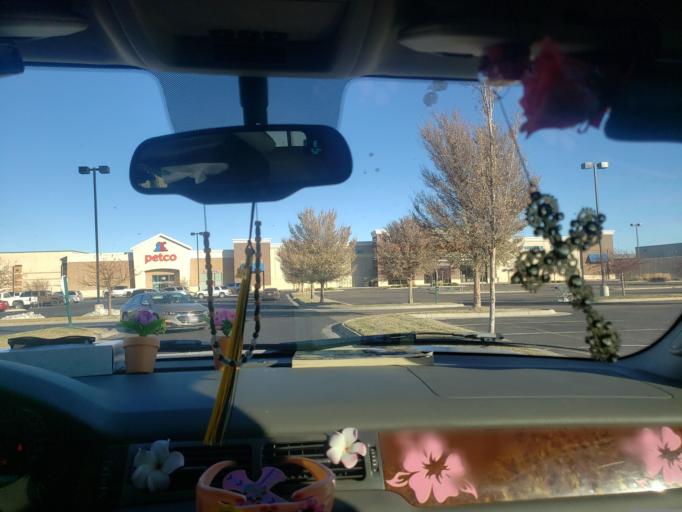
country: US
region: Kansas
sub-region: Finney County
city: Garden City
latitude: 37.9780
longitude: -100.8361
